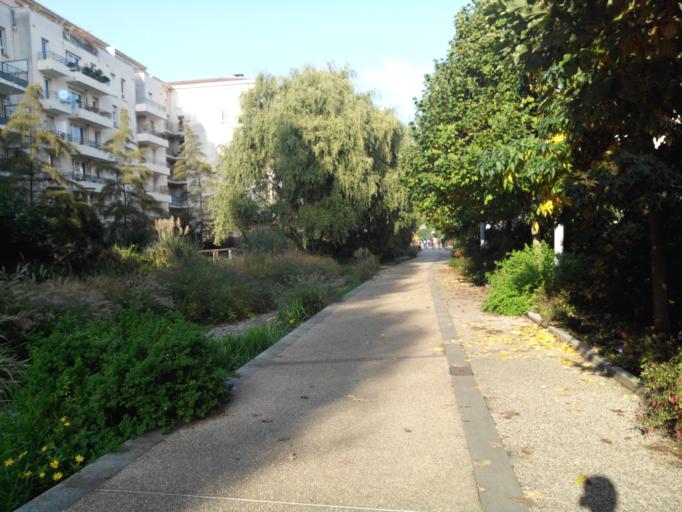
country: FR
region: Ile-de-France
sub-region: Departement du Val-de-Marne
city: Cachan
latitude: 48.7912
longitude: 2.3328
